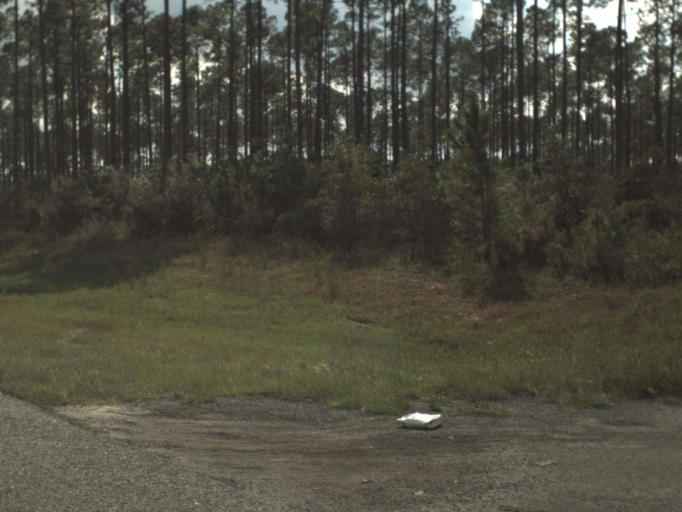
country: US
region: Florida
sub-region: Bay County
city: Laguna Beach
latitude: 30.4273
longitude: -85.8751
